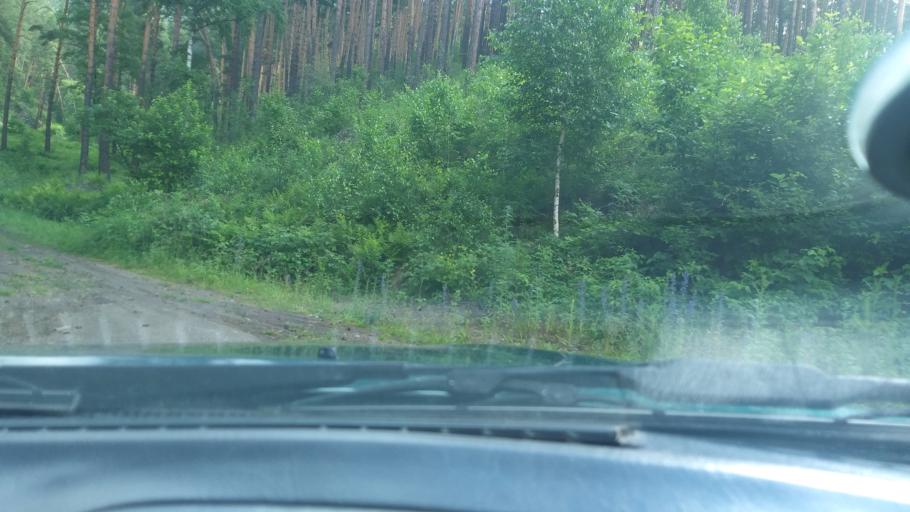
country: RU
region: Altay
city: Chemal
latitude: 51.3908
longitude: 86.0523
